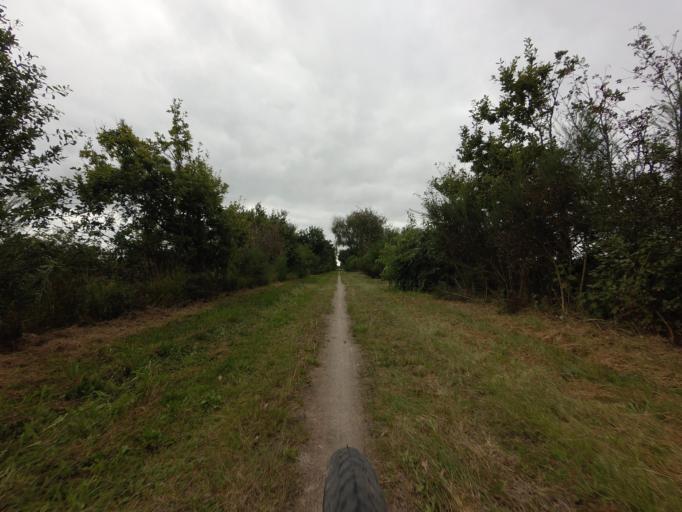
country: DK
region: Central Jutland
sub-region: Ikast-Brande Kommune
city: Brande
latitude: 55.8986
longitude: 9.0743
